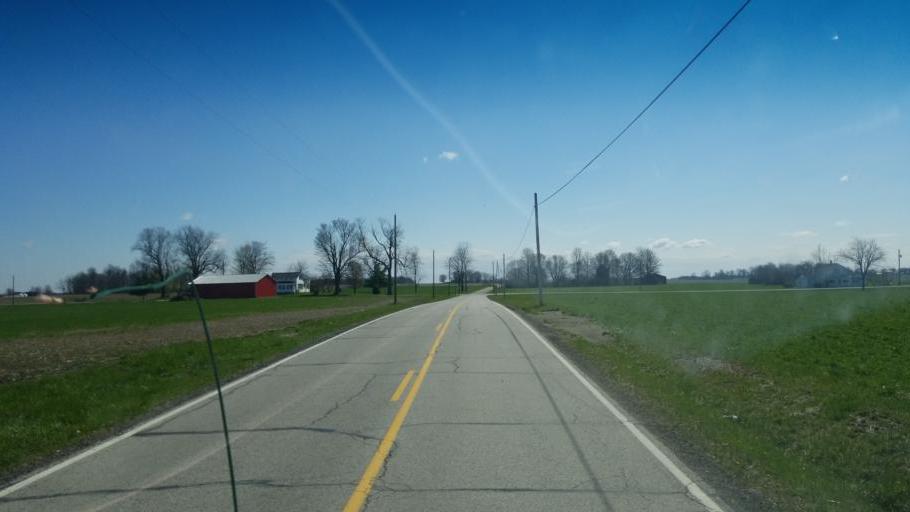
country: US
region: Ohio
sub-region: Crawford County
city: Bucyrus
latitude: 40.8654
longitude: -82.9423
